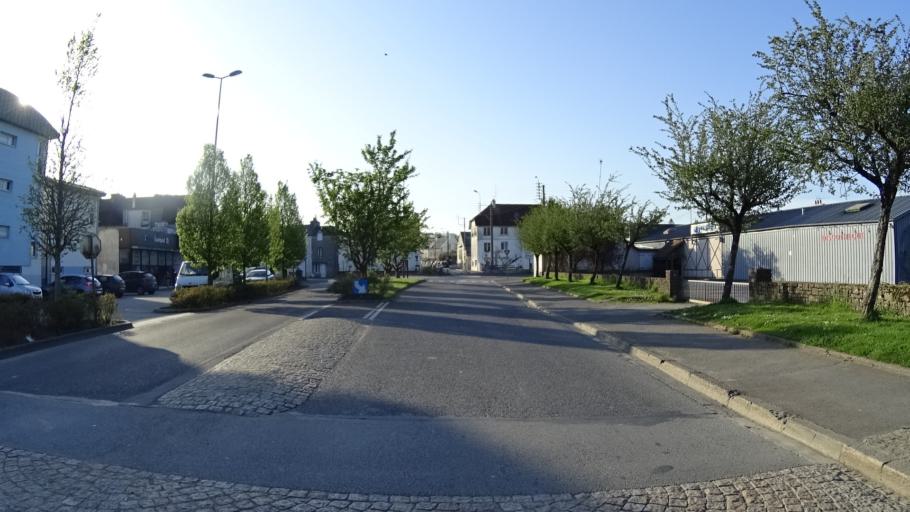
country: FR
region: Brittany
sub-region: Departement du Finistere
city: Landerneau
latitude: 48.4535
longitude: -4.2439
